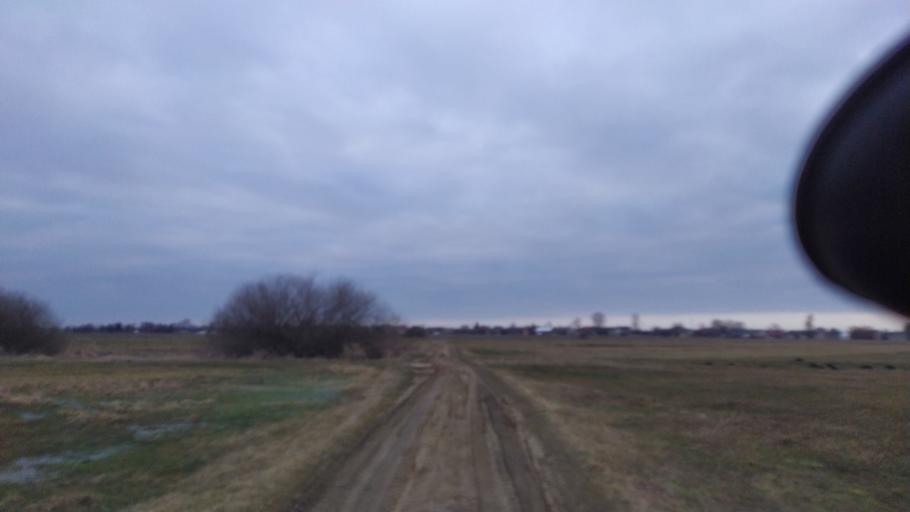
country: PL
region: Lublin Voivodeship
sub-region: Powiat lubartowski
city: Abramow
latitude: 51.4351
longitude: 22.2939
